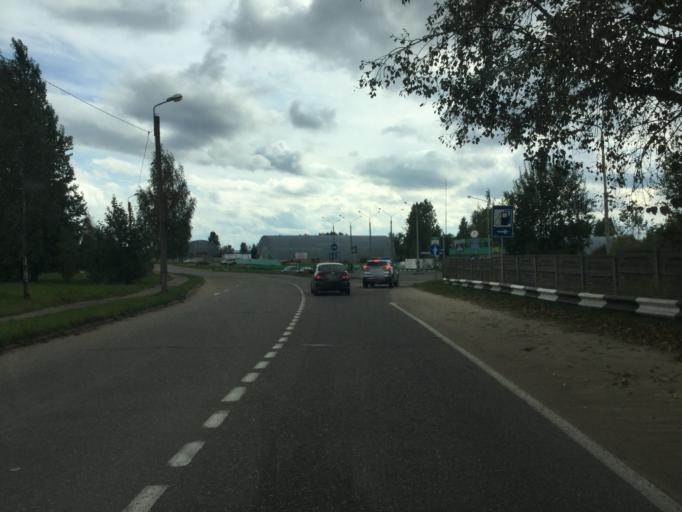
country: BY
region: Vitebsk
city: Vitebsk
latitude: 55.1713
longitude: 30.2480
